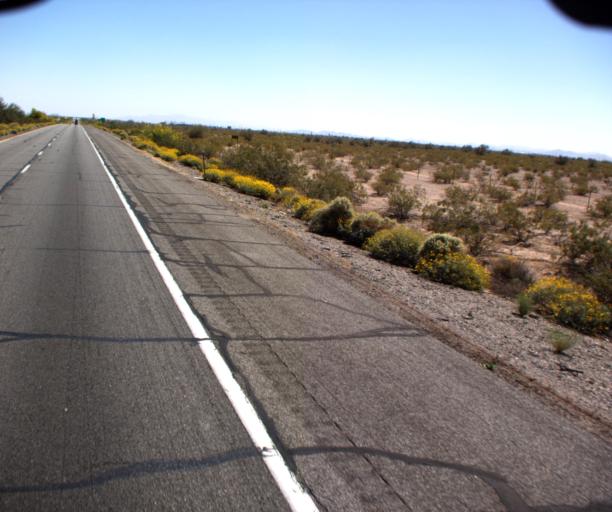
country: US
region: Arizona
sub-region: Maricopa County
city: Buckeye
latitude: 33.4683
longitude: -112.8074
